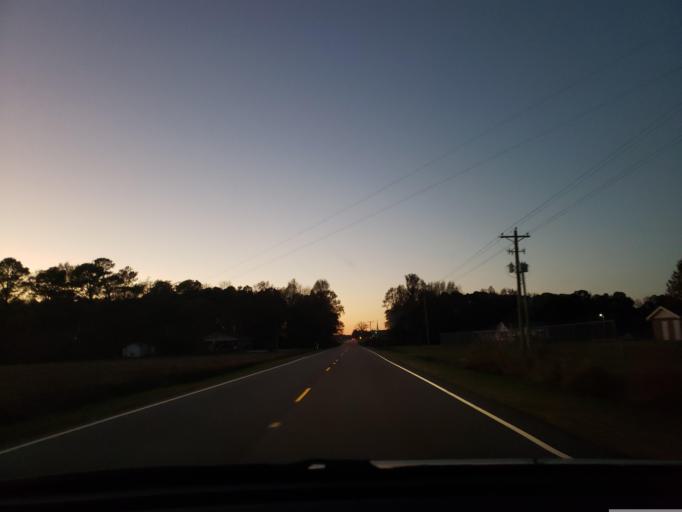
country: US
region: North Carolina
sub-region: Duplin County
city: Kenansville
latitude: 34.9007
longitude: -77.9148
